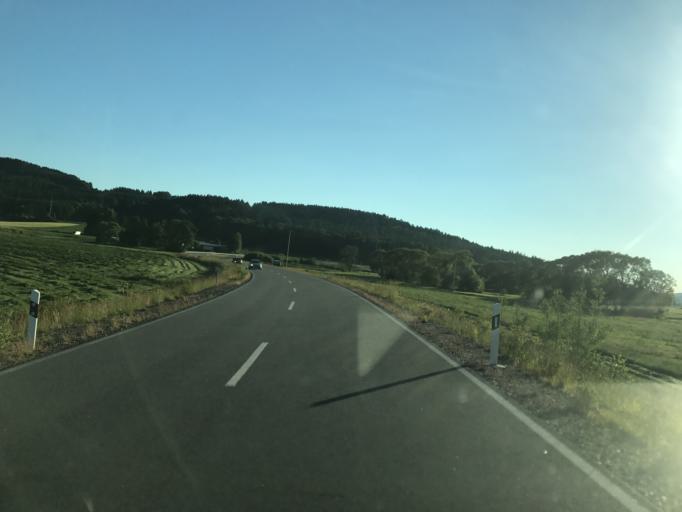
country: DE
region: Bavaria
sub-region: Upper Palatinate
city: Waldmunchen
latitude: 49.3800
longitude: 12.6862
